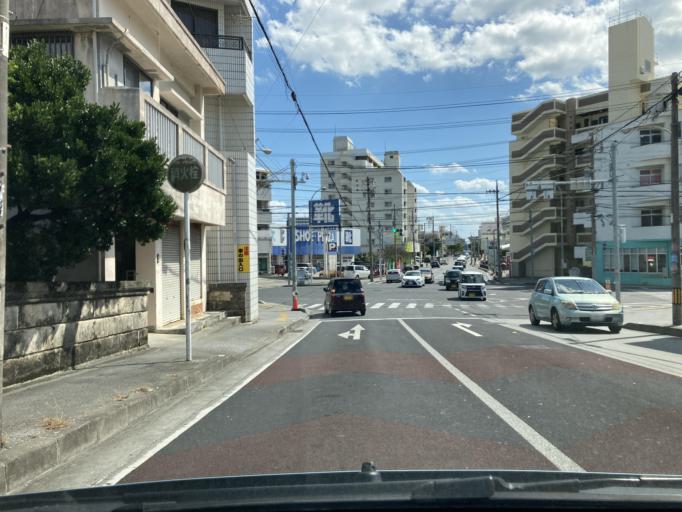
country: JP
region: Okinawa
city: Tomigusuku
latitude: 26.1965
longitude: 127.7045
